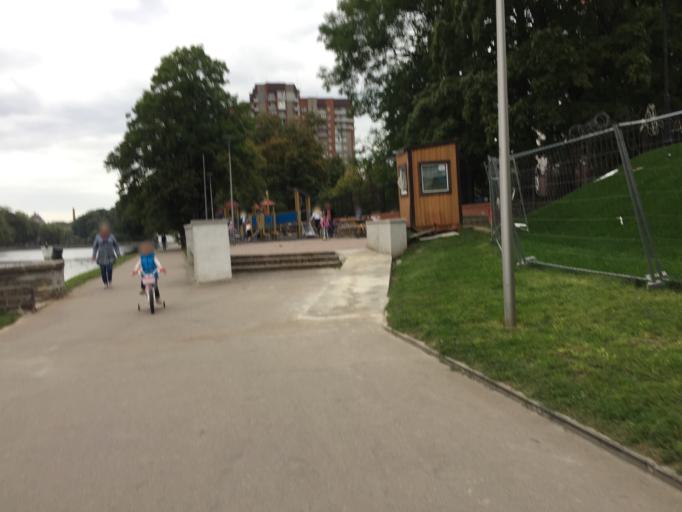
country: RU
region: Kaliningrad
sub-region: Gorod Kaliningrad
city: Kaliningrad
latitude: 54.7137
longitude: 20.5168
